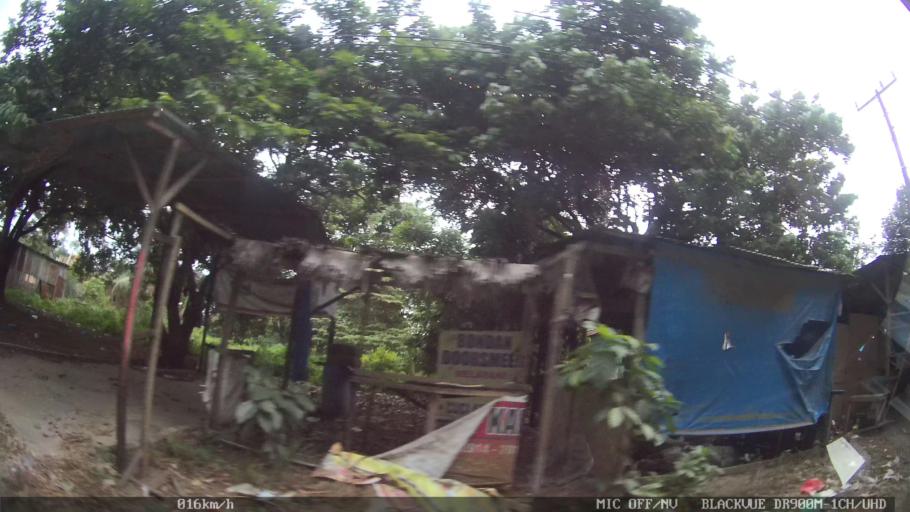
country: ID
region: North Sumatra
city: Sunggal
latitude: 3.5610
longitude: 98.5849
